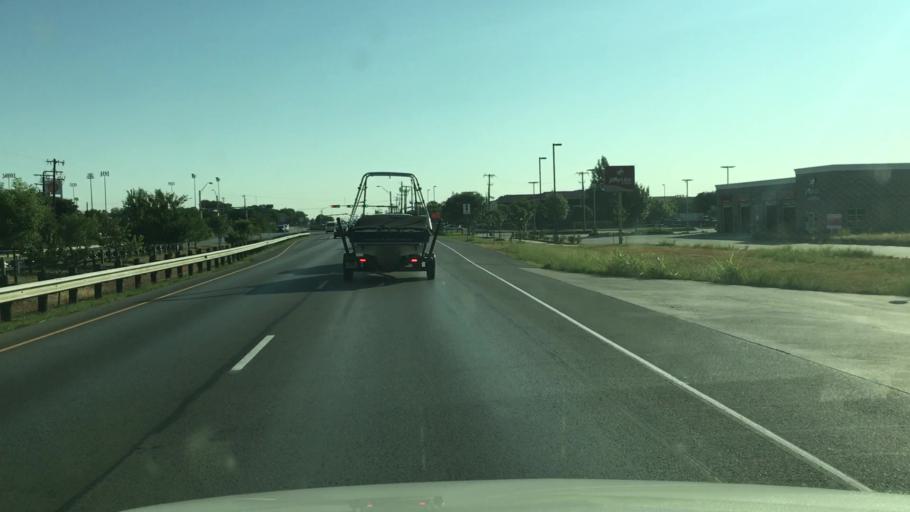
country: US
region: Texas
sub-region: Johnson County
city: Burleson
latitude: 32.5234
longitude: -97.3455
